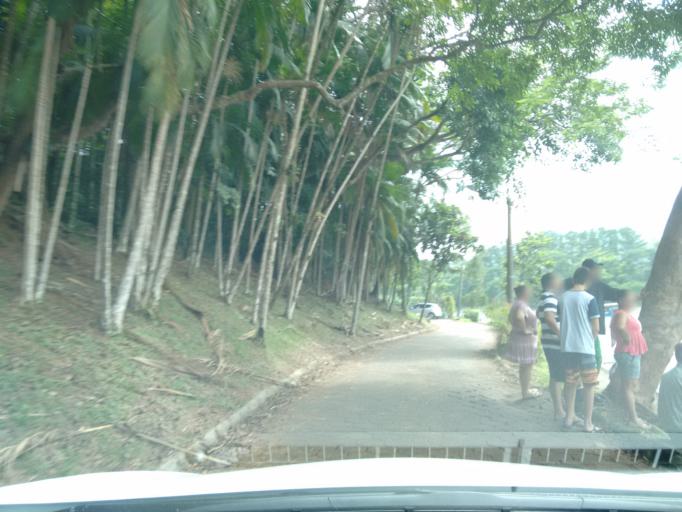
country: BR
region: Santa Catarina
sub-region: Jaragua Do Sul
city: Jaragua do Sul
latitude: -26.5052
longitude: -49.1277
